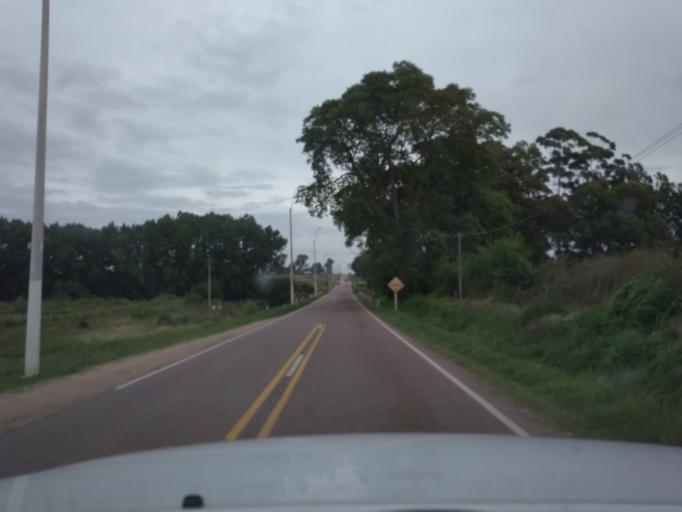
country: UY
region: Canelones
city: Tala
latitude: -34.3542
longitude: -55.7703
